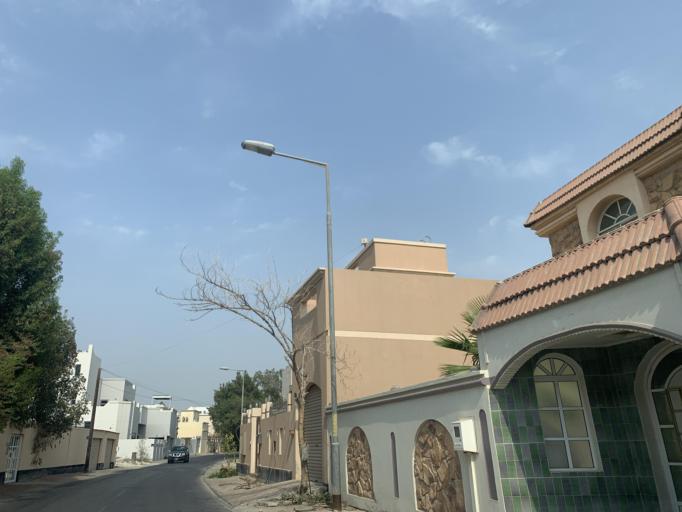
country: BH
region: Manama
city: Jidd Hafs
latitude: 26.2154
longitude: 50.4892
